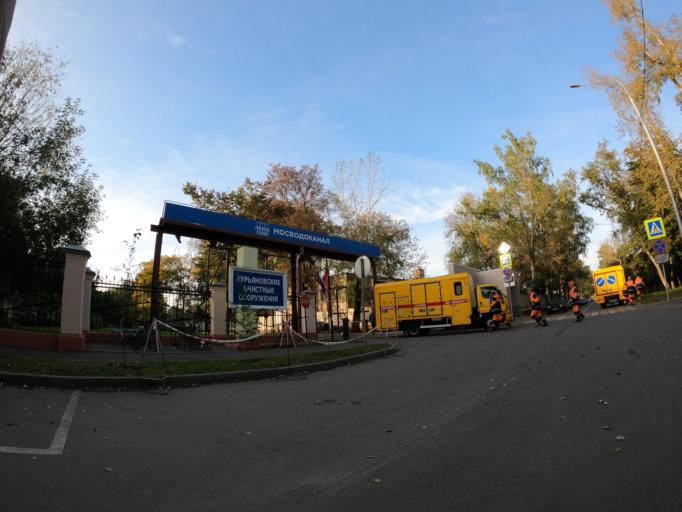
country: RU
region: Moskovskaya
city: Kur'yanovo
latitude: 55.6575
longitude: 37.6960
